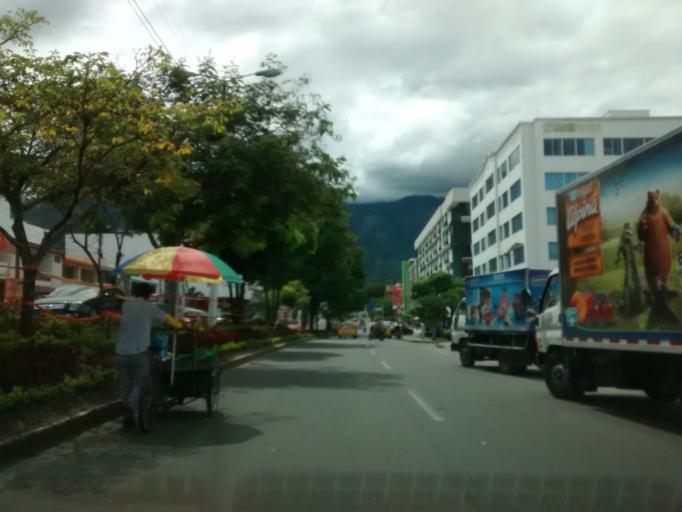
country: CO
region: Tolima
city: Ibague
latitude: 4.4373
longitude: -75.2033
